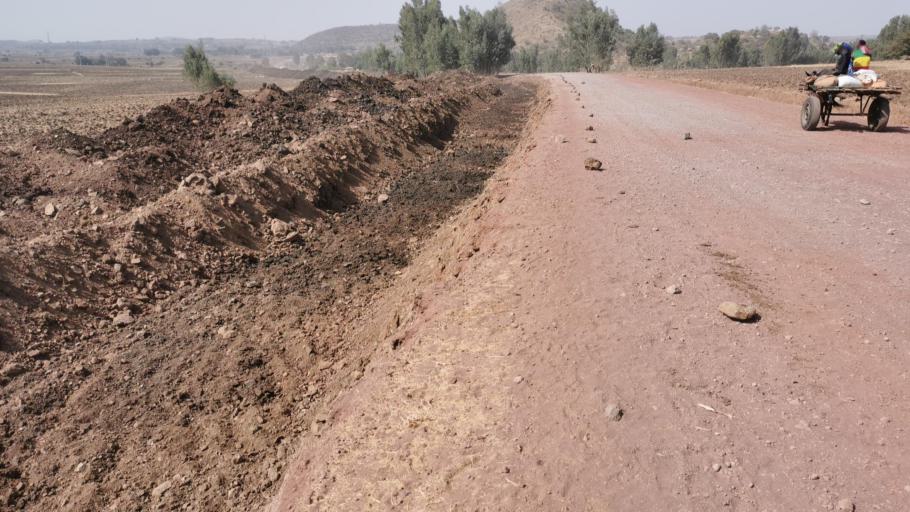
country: ET
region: Amhara
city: Bahir Dar
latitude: 11.8437
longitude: 37.0028
